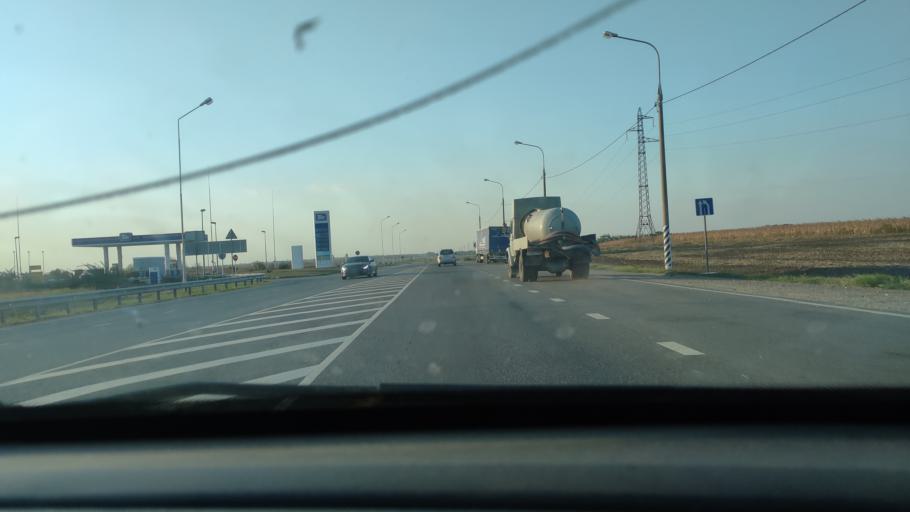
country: RU
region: Krasnodarskiy
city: Kanevskaya
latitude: 46.0783
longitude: 39.0139
